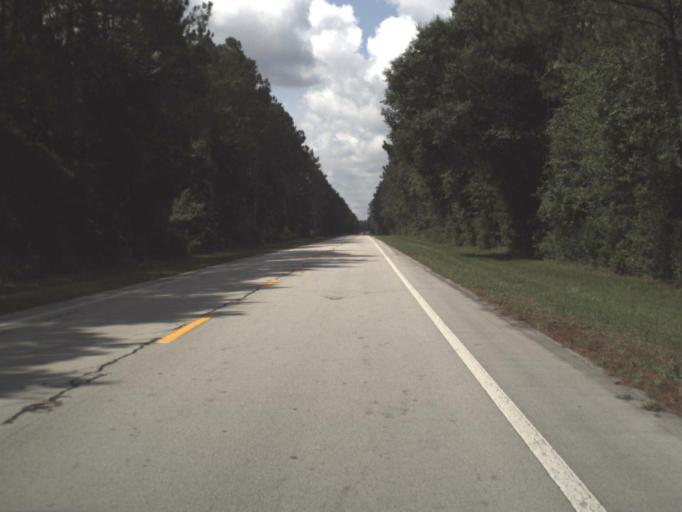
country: US
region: Florida
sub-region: Baker County
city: Macclenny
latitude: 30.1624
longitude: -82.1845
